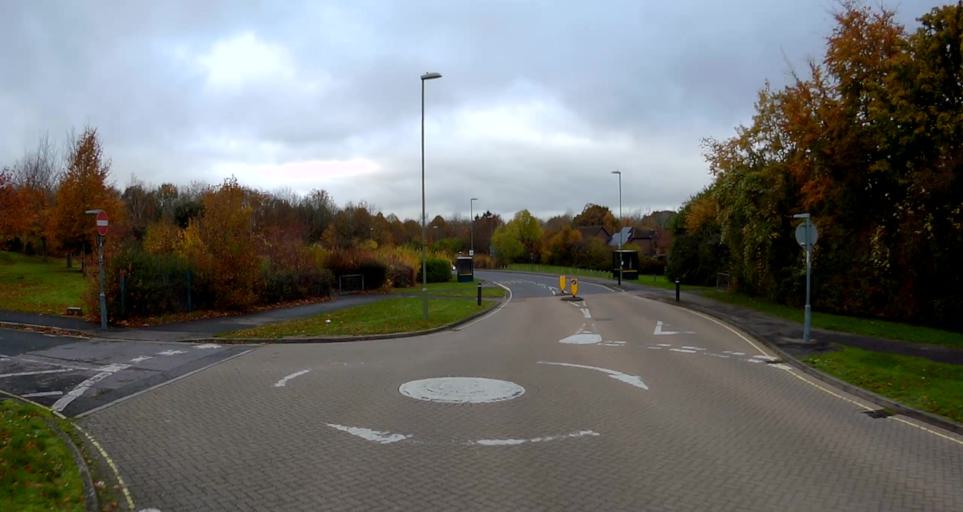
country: GB
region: England
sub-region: Hampshire
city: Basingstoke
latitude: 51.2349
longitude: -1.1300
